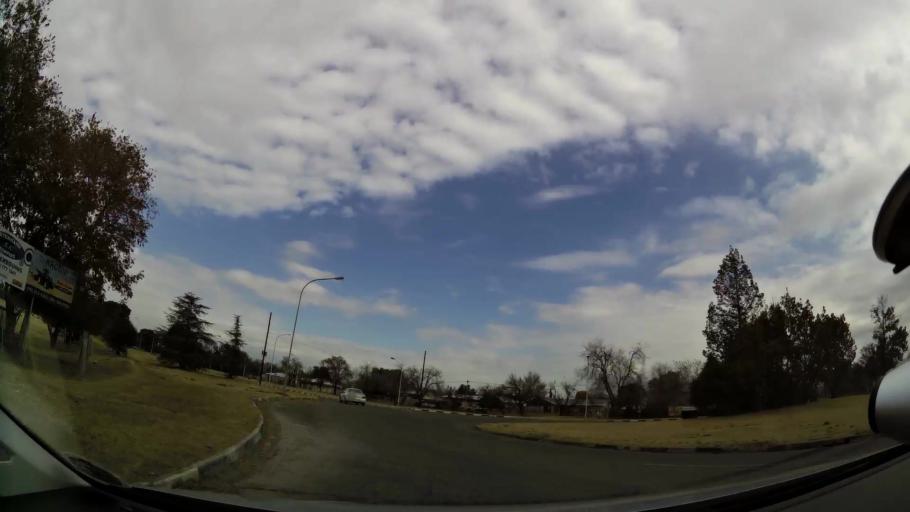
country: ZA
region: Orange Free State
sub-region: Fezile Dabi District Municipality
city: Kroonstad
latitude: -27.6324
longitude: 27.2336
